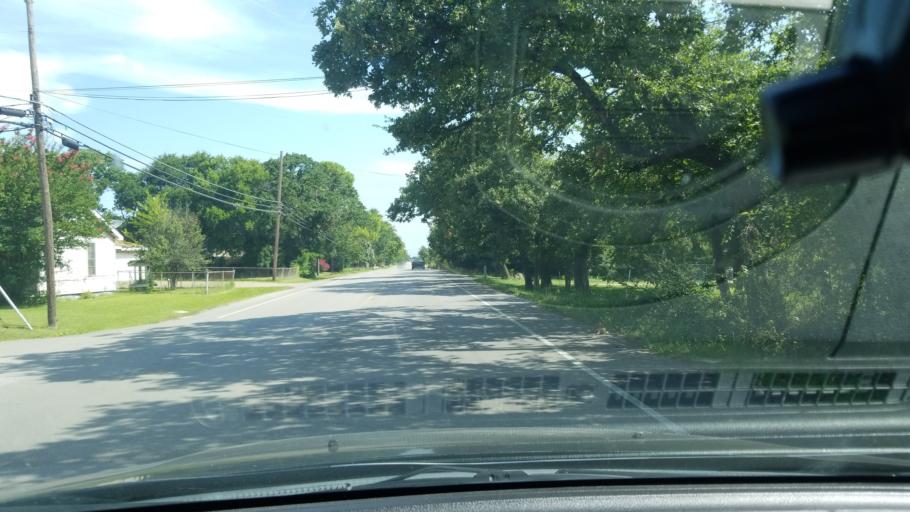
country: US
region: Texas
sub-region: Dallas County
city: Balch Springs
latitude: 32.7243
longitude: -96.6312
